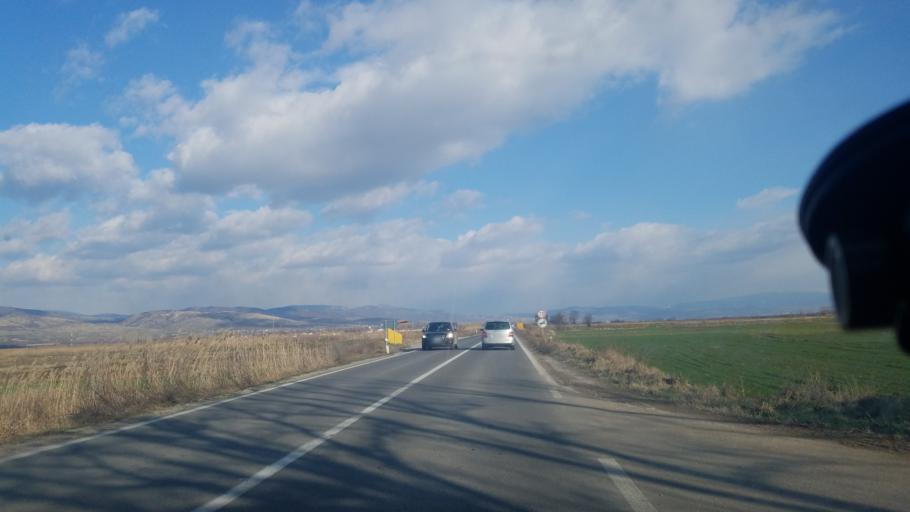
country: MK
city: Obleshevo
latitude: 41.8729
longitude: 22.3166
